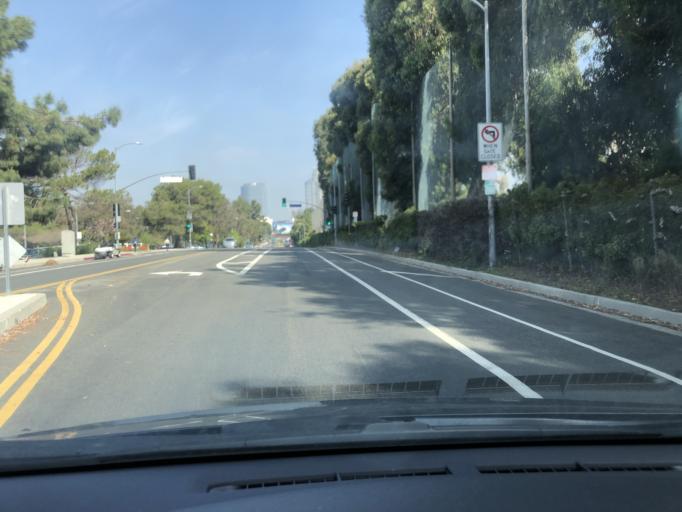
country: US
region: California
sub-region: Los Angeles County
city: Century City
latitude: 34.0465
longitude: -118.4077
